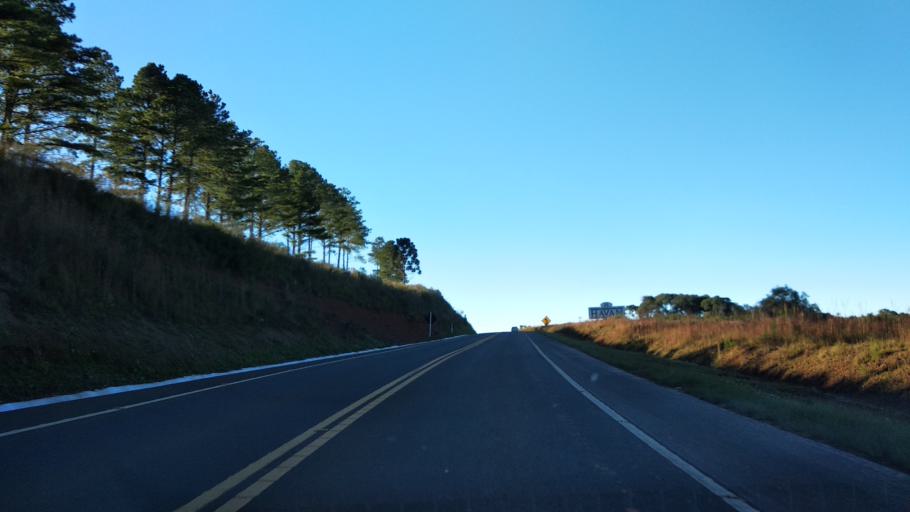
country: BR
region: Santa Catarina
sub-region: Lages
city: Lages
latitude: -27.7911
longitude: -50.4081
